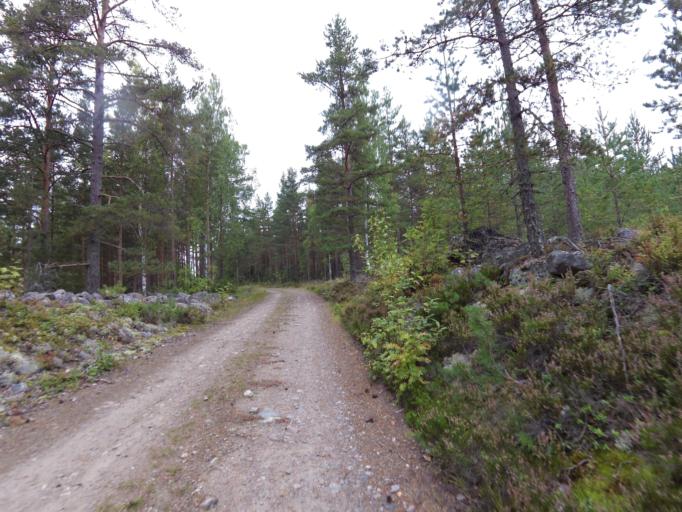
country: SE
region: Gaevleborg
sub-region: Gavle Kommun
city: Valbo
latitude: 60.7518
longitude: 16.9756
